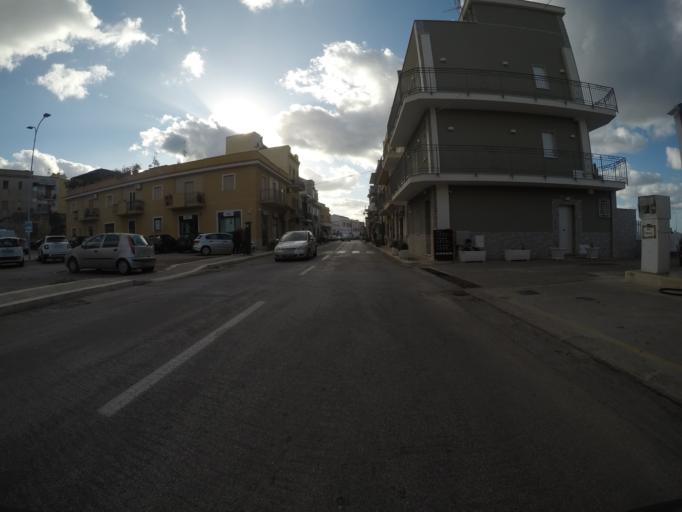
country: IT
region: Sicily
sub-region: Palermo
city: Isola delle Femmine
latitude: 38.1986
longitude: 13.2505
